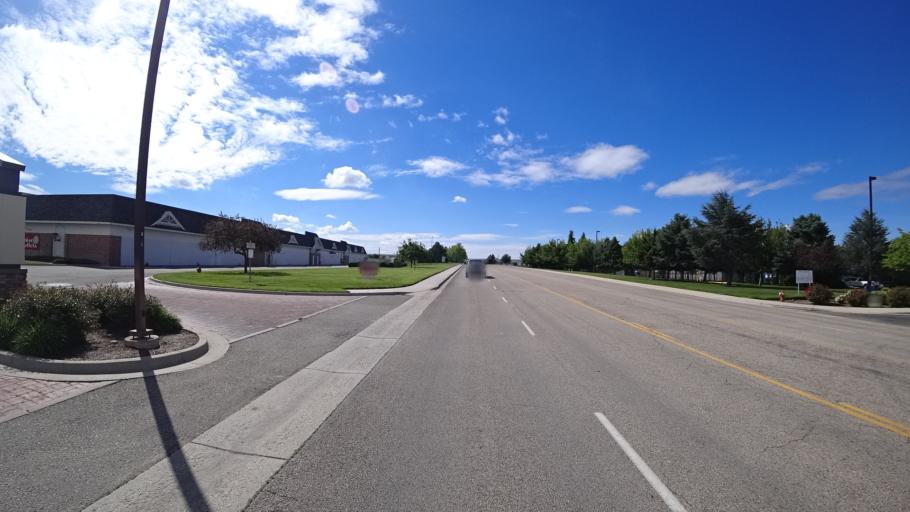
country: US
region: Idaho
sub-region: Ada County
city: Boise
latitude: 43.5384
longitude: -116.1627
